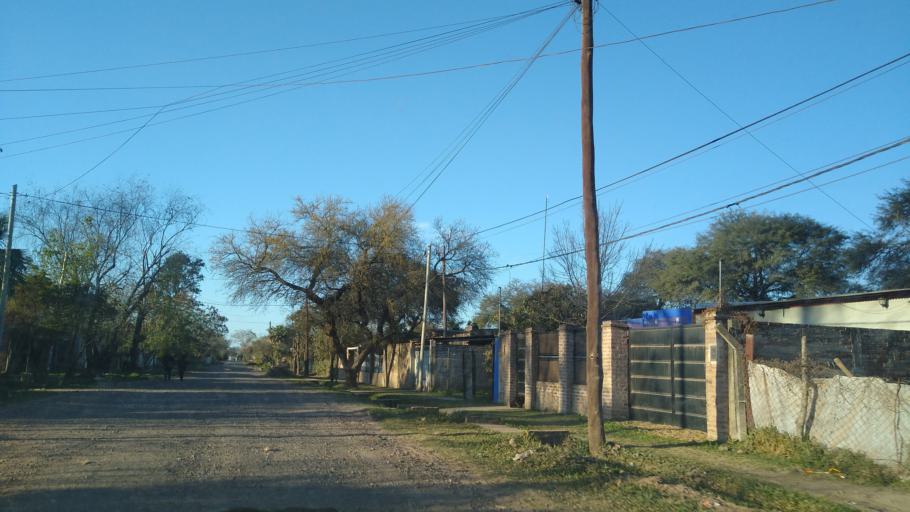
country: AR
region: Chaco
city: Barranqueras
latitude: -27.4704
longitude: -58.9486
